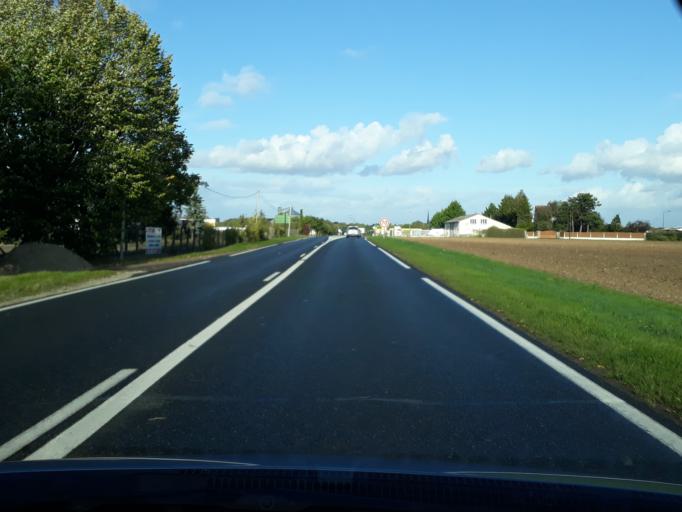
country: FR
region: Centre
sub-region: Departement du Loiret
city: Pithiviers
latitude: 48.1567
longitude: 2.2304
